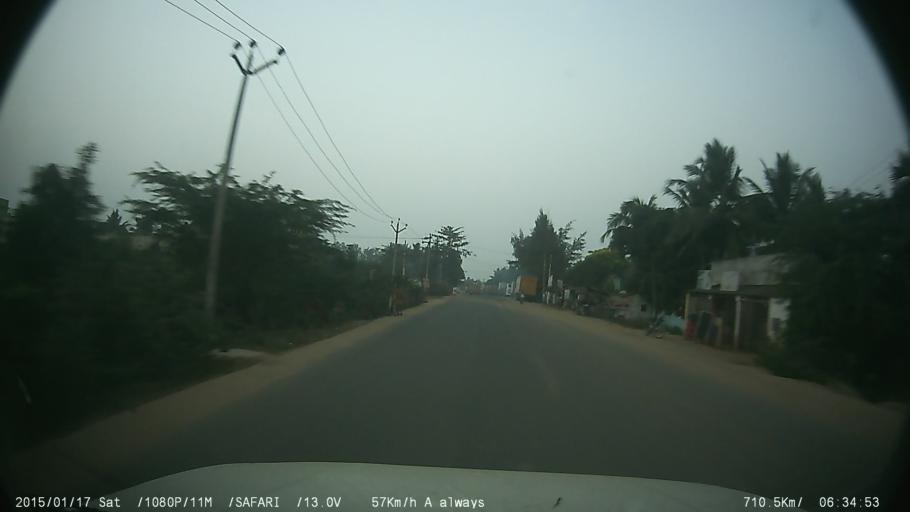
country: IN
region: Tamil Nadu
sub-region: Kancheepuram
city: Sriperumbudur
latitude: 12.9532
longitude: 79.9404
